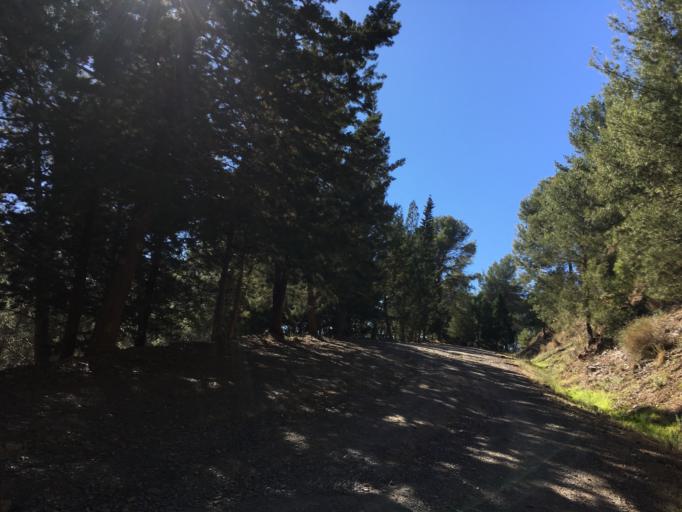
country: ES
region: Andalusia
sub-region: Provincia de Malaga
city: Malaga
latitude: 36.7993
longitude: -4.3989
